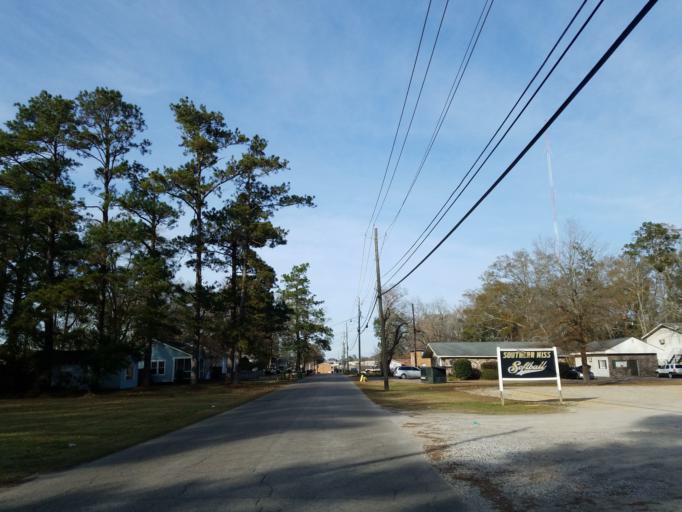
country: US
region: Mississippi
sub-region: Forrest County
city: Hattiesburg
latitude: 31.3332
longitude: -89.3278
